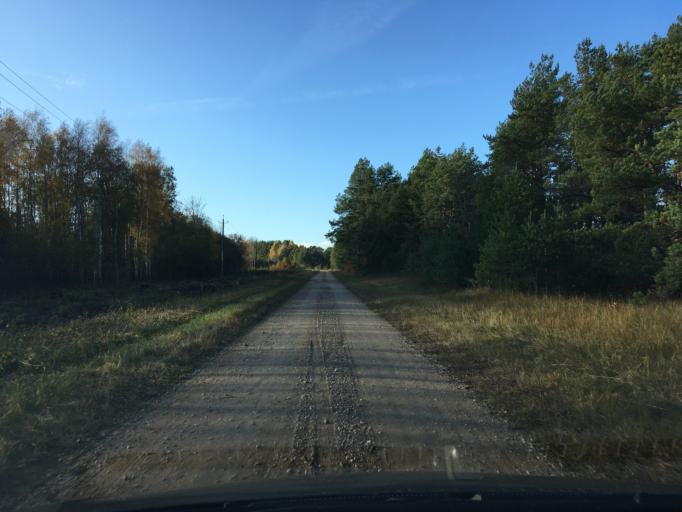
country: EE
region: Laeaene
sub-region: Lihula vald
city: Lihula
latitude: 58.5659
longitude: 23.7673
